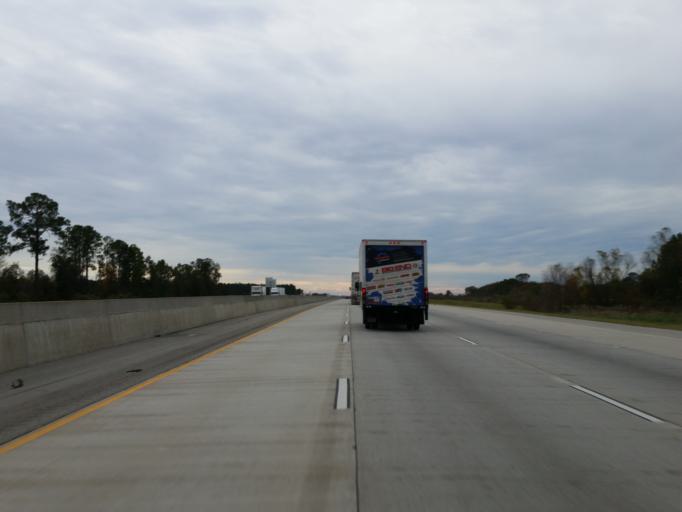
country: US
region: Georgia
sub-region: Tift County
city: Unionville
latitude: 31.3483
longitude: -83.4876
